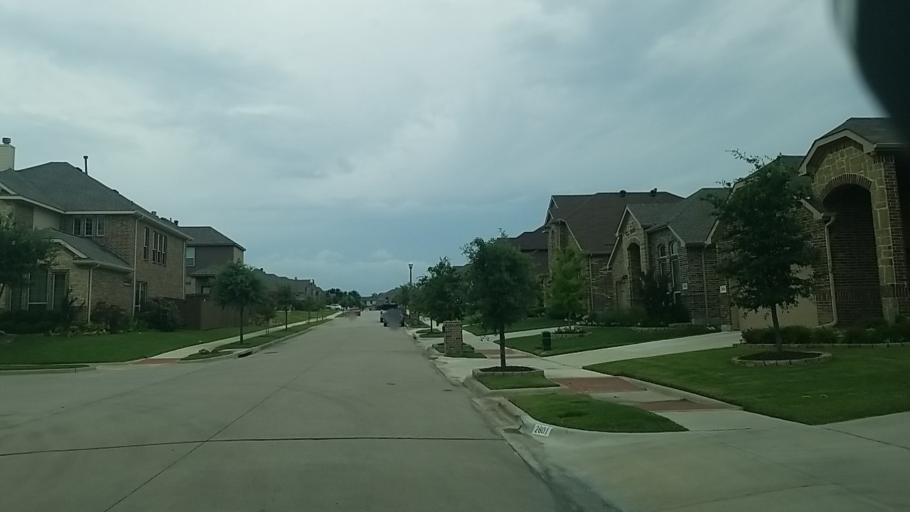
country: US
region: Texas
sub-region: Denton County
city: Corinth
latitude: 33.1736
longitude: -97.1042
